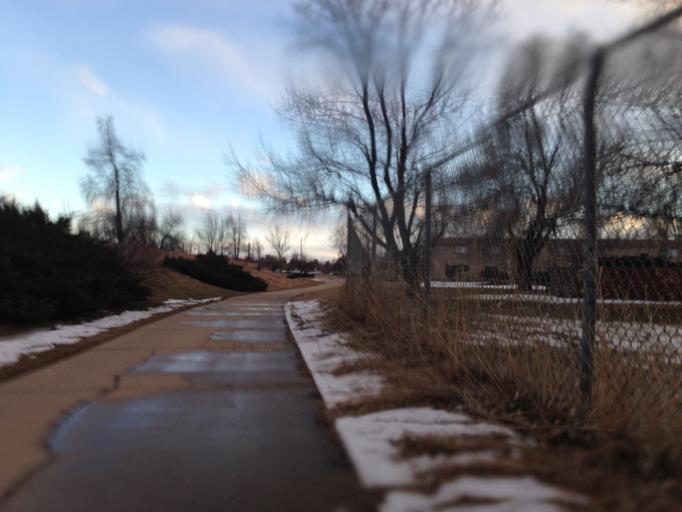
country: US
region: Colorado
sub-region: Boulder County
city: Boulder
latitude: 40.0023
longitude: -105.2350
